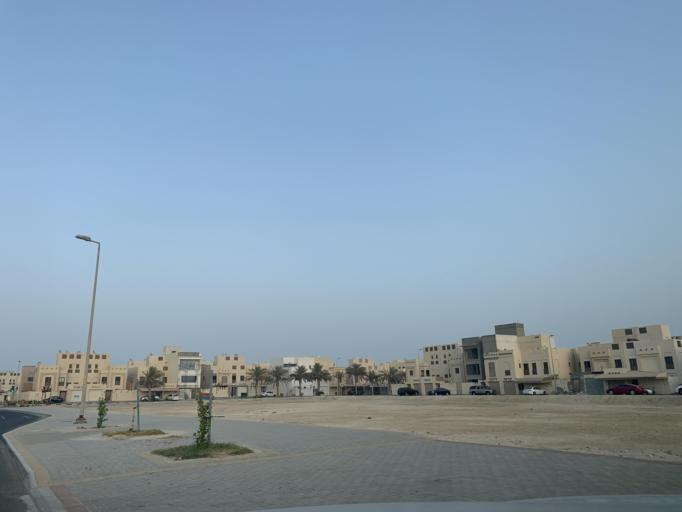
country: BH
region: Manama
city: Jidd Hafs
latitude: 26.2224
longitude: 50.4402
